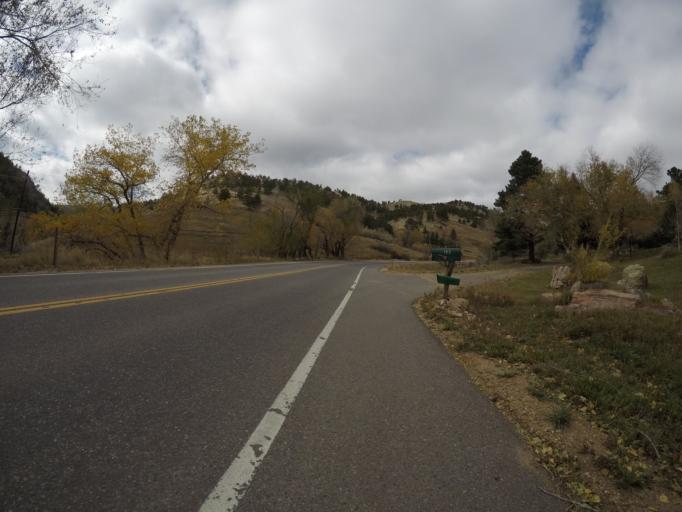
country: US
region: Colorado
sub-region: Boulder County
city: Boulder
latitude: 40.0652
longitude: -105.3013
